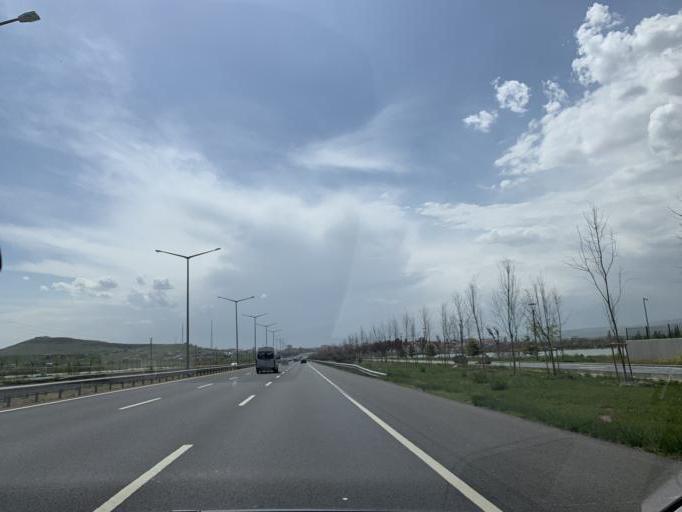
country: TR
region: Ankara
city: Temelli
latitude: 39.7299
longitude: 32.3710
